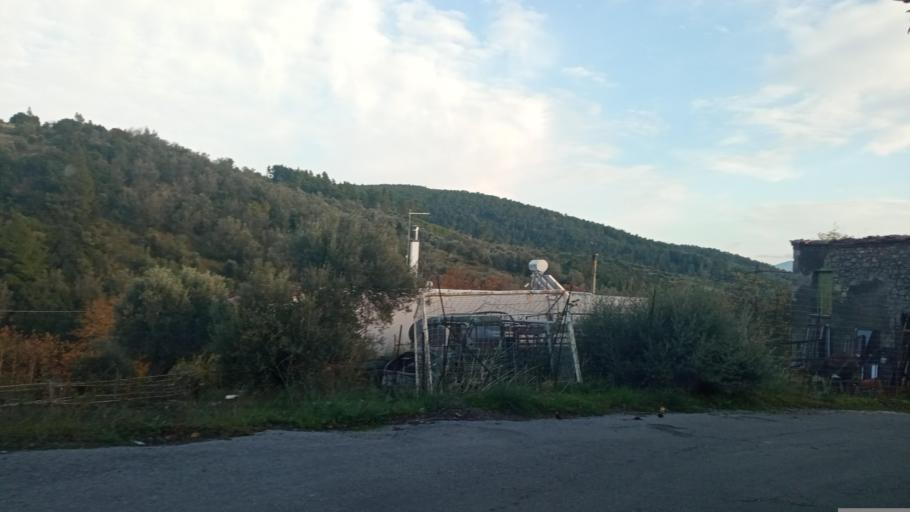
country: GR
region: Central Greece
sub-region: Nomos Evvoias
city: Psachna
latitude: 38.6199
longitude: 23.7363
